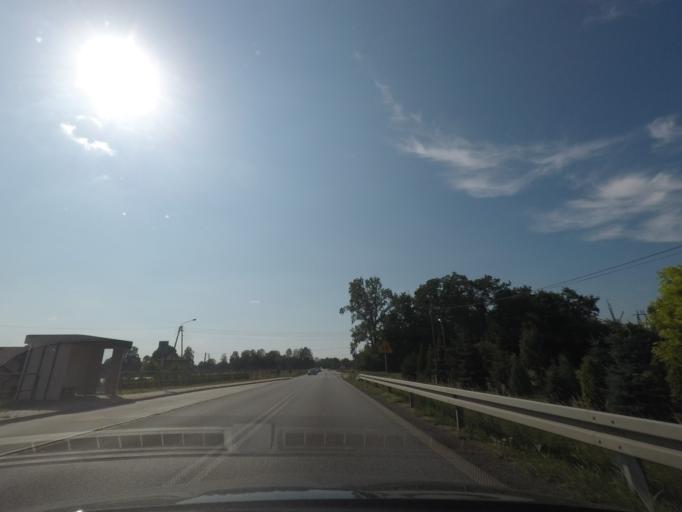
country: PL
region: Silesian Voivodeship
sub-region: Powiat pszczynski
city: Kryry
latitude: 50.0263
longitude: 18.8329
